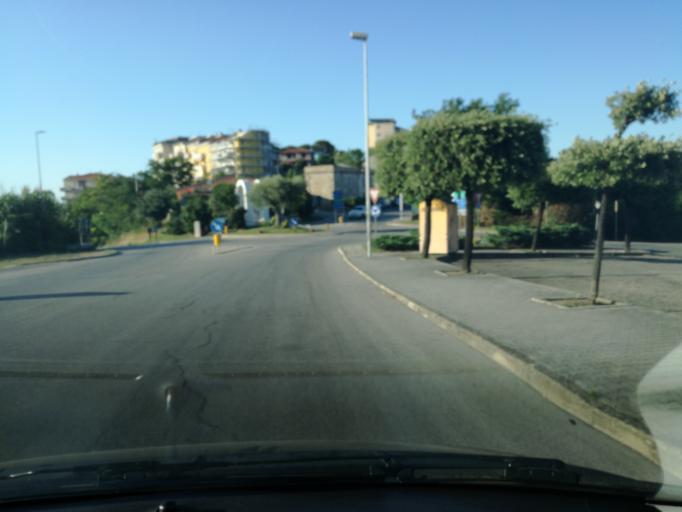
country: IT
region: Molise
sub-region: Provincia di Campobasso
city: Guglionesi
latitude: 41.9175
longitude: 14.9138
